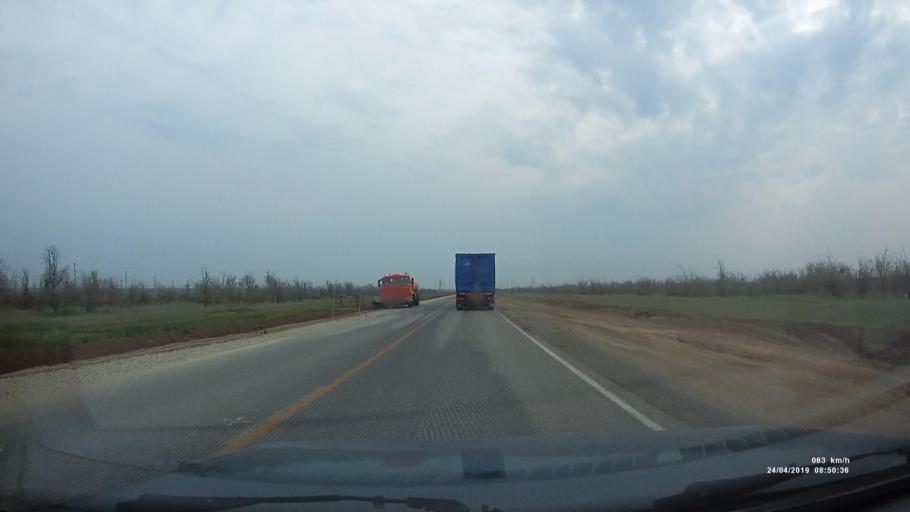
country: RU
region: Kalmykiya
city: Arshan'
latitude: 46.2627
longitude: 44.1391
